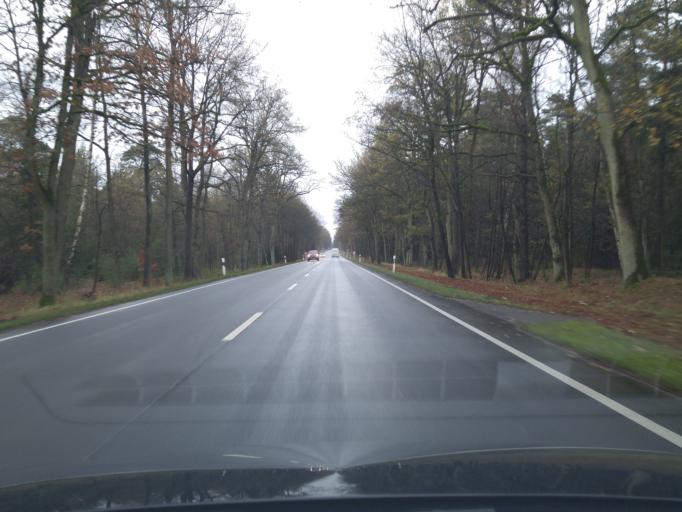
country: DE
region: Lower Saxony
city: Dedelstorf
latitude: 52.6827
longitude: 10.4717
